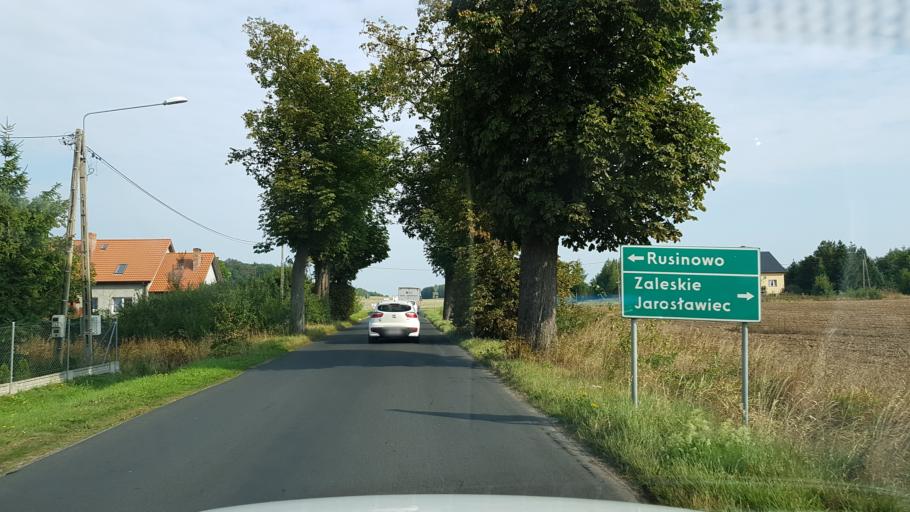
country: PL
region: West Pomeranian Voivodeship
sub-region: Powiat slawienski
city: Slawno
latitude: 54.5080
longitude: 16.5741
